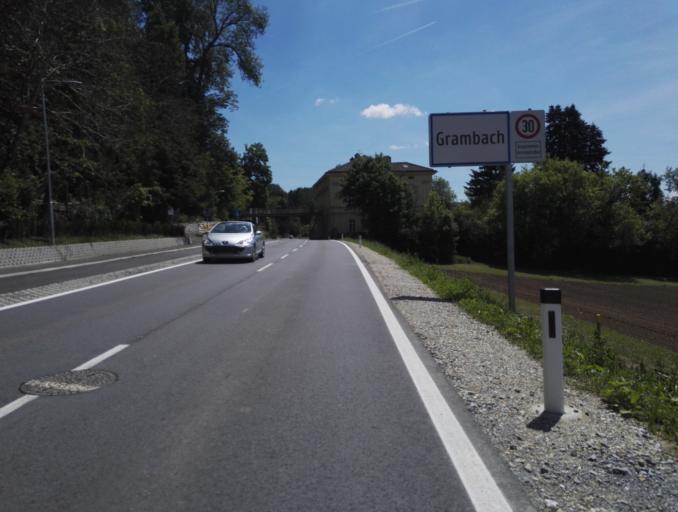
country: AT
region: Styria
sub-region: Politischer Bezirk Graz-Umgebung
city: Grambach
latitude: 47.0215
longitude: 15.5004
